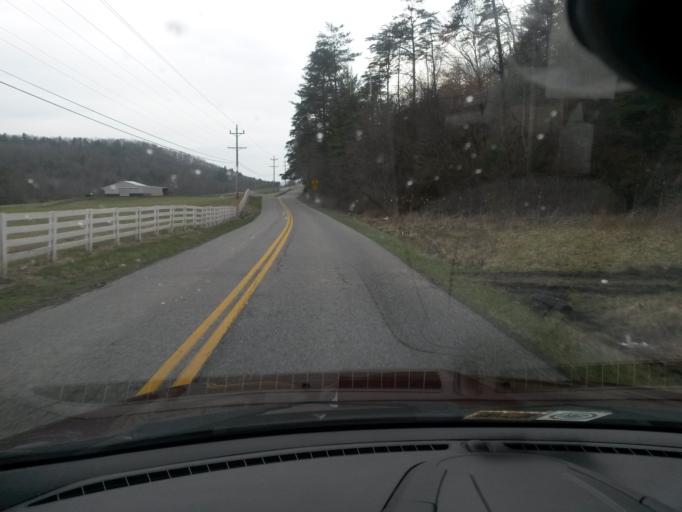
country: US
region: Virginia
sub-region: Bath County
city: Warm Springs
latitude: 37.9885
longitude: -79.8984
